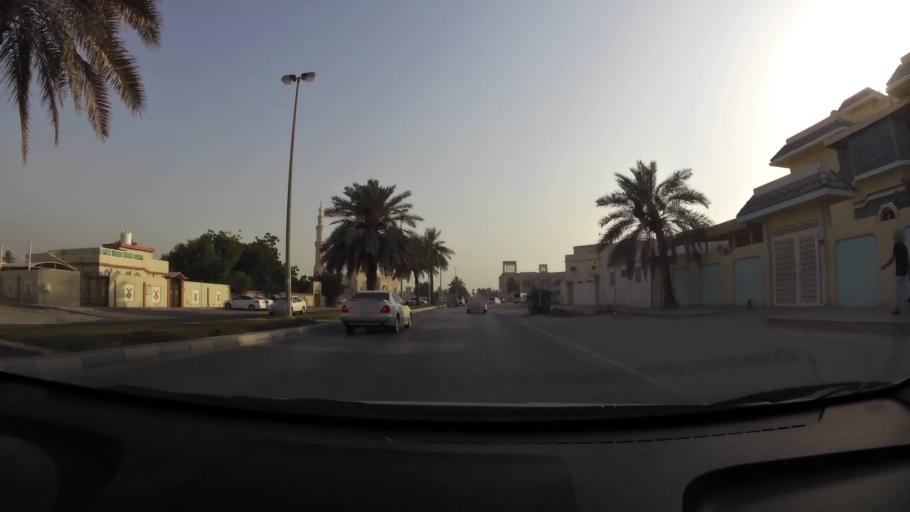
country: AE
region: Ajman
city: Ajman
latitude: 25.3729
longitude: 55.4287
